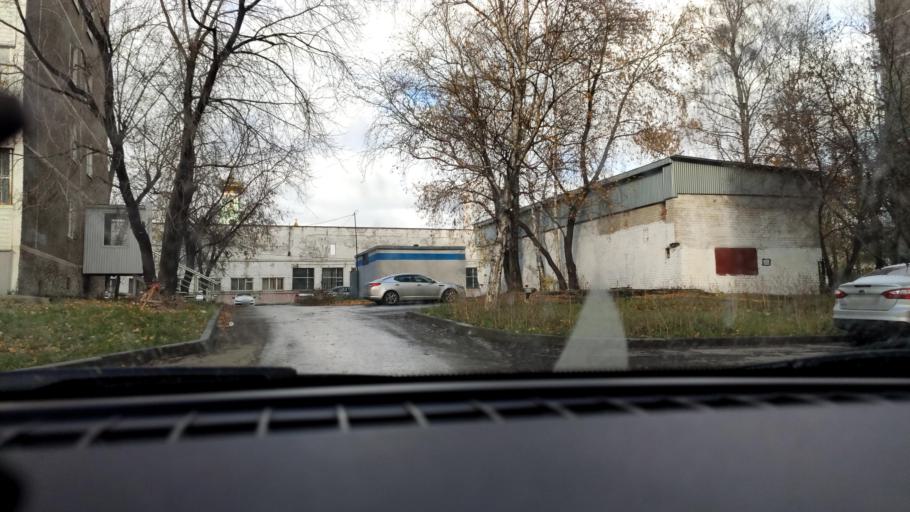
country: RU
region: Perm
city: Perm
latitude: 58.0103
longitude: 56.2180
